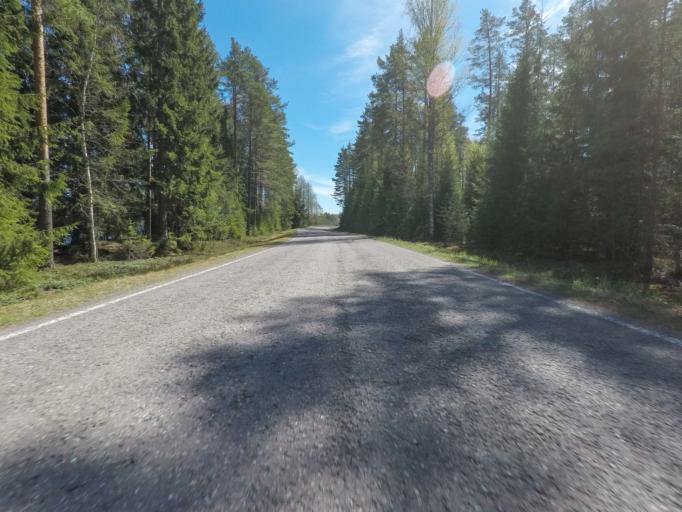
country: FI
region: Uusimaa
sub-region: Helsinki
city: Kaerkoelae
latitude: 60.6200
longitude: 23.8436
